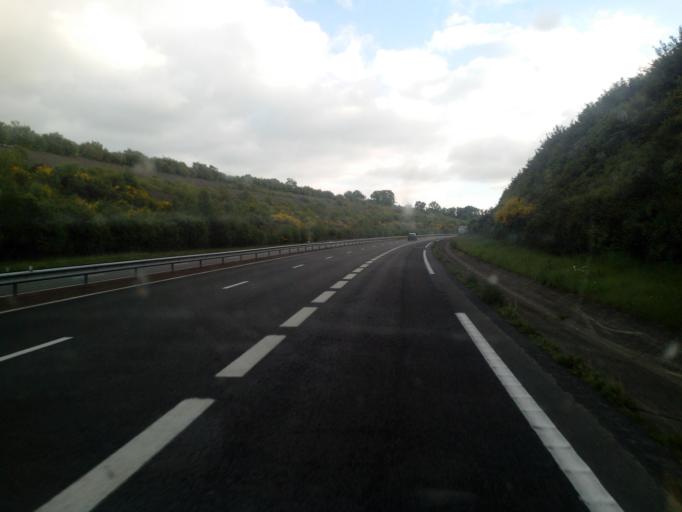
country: FR
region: Lower Normandy
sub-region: Departement de la Manche
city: Tessy-sur-Vire
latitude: 48.9267
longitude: -1.0755
